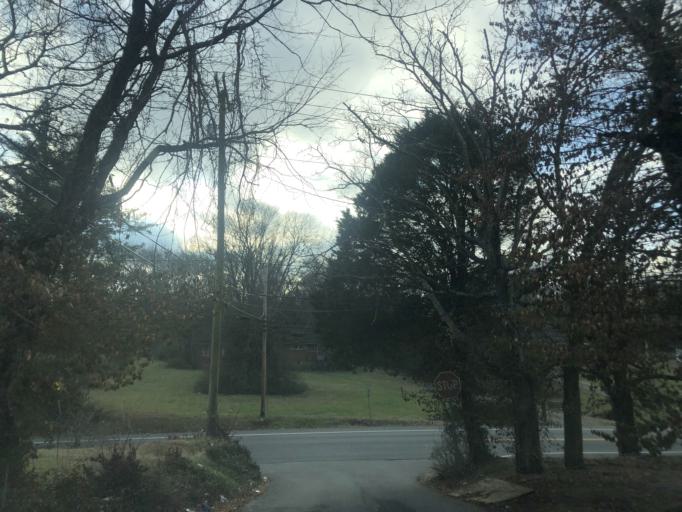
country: US
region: Tennessee
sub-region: Davidson County
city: Nashville
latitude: 36.2125
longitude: -86.7982
